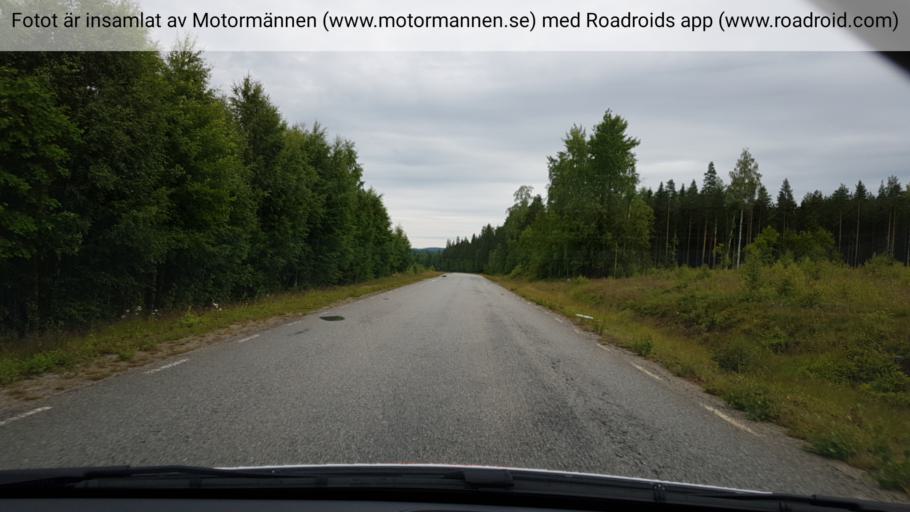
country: SE
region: Vaesterbotten
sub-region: Vannas Kommun
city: Vannasby
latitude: 64.0122
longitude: 19.9280
